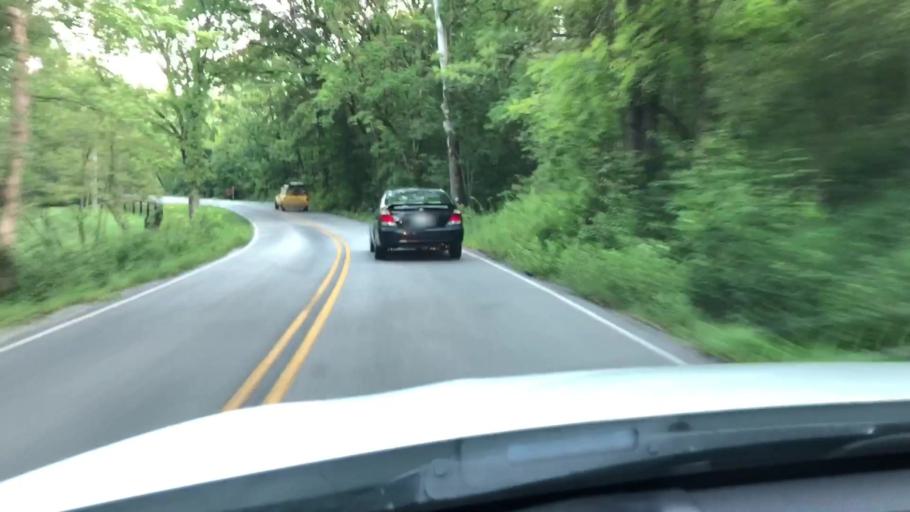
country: US
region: Kentucky
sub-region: Jefferson County
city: Middletown
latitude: 38.1924
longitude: -85.4879
